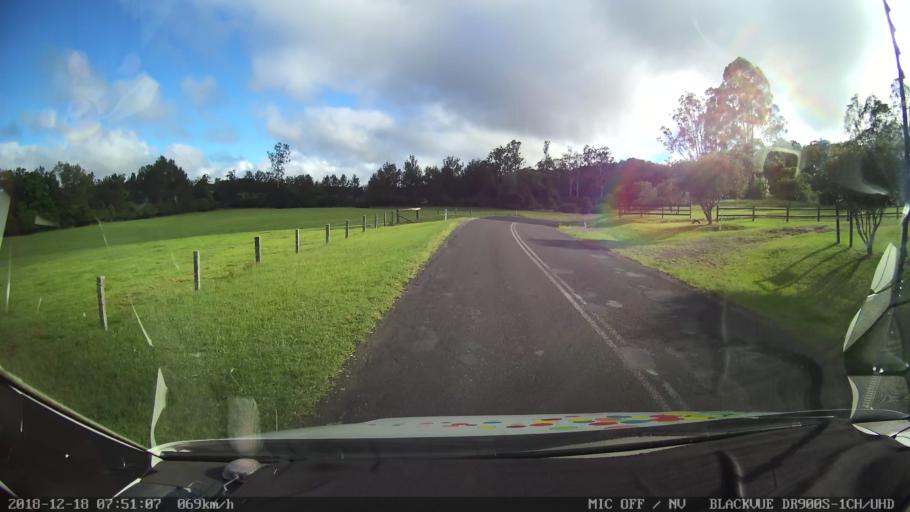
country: AU
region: New South Wales
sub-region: Kyogle
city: Kyogle
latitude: -28.4393
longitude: 152.5760
